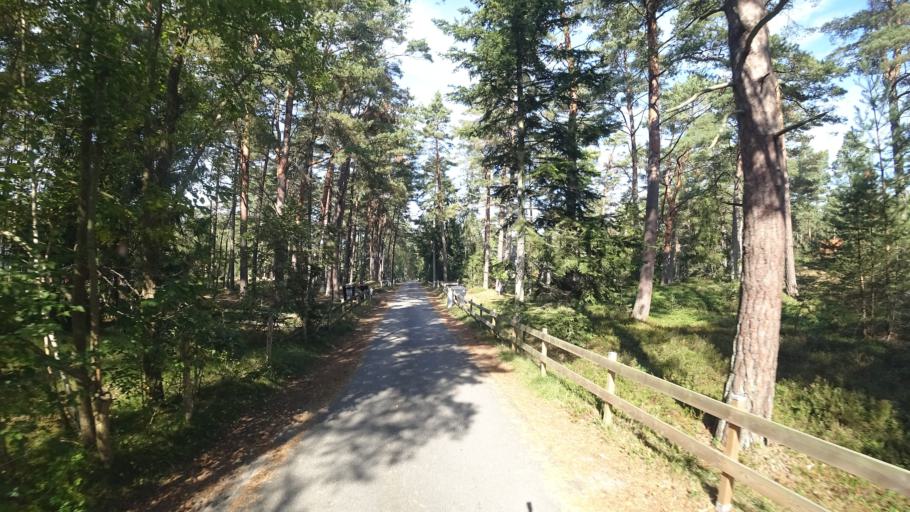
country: SE
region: Skane
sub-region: Kristianstads Kommun
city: Ahus
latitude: 55.9141
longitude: 14.3086
